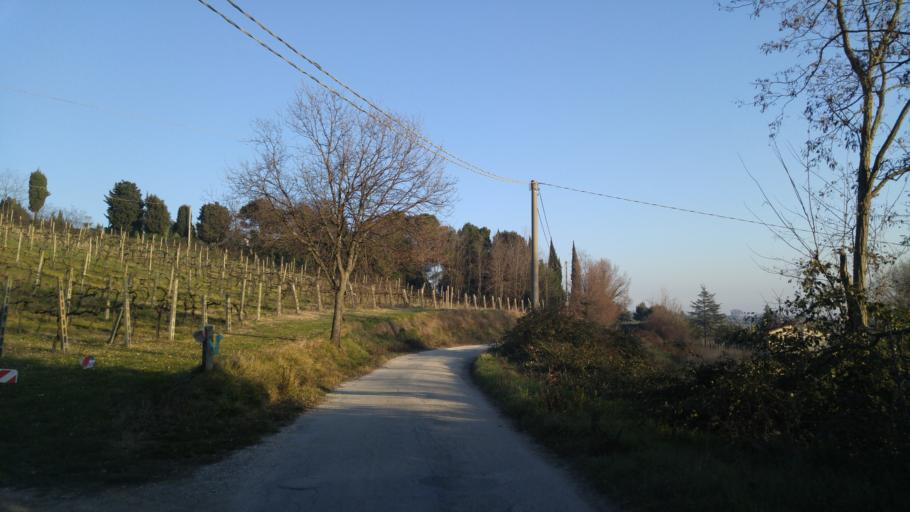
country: IT
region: The Marches
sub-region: Provincia di Pesaro e Urbino
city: Fenile
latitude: 43.8619
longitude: 12.9512
